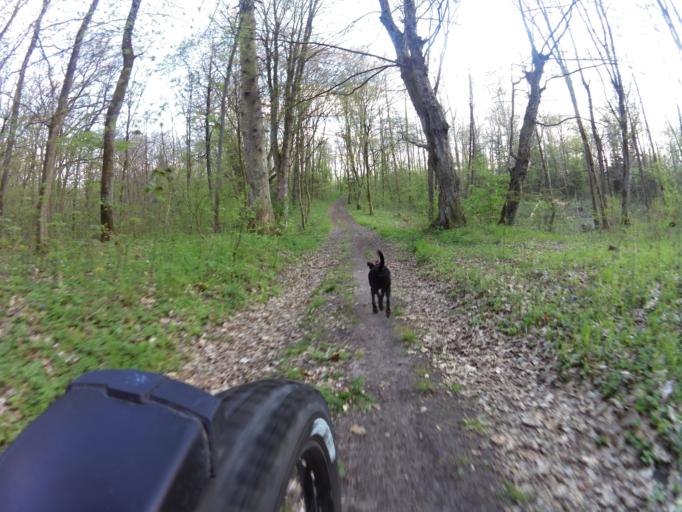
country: PL
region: West Pomeranian Voivodeship
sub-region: Powiat gryficki
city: Ploty
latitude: 53.7759
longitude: 15.2516
